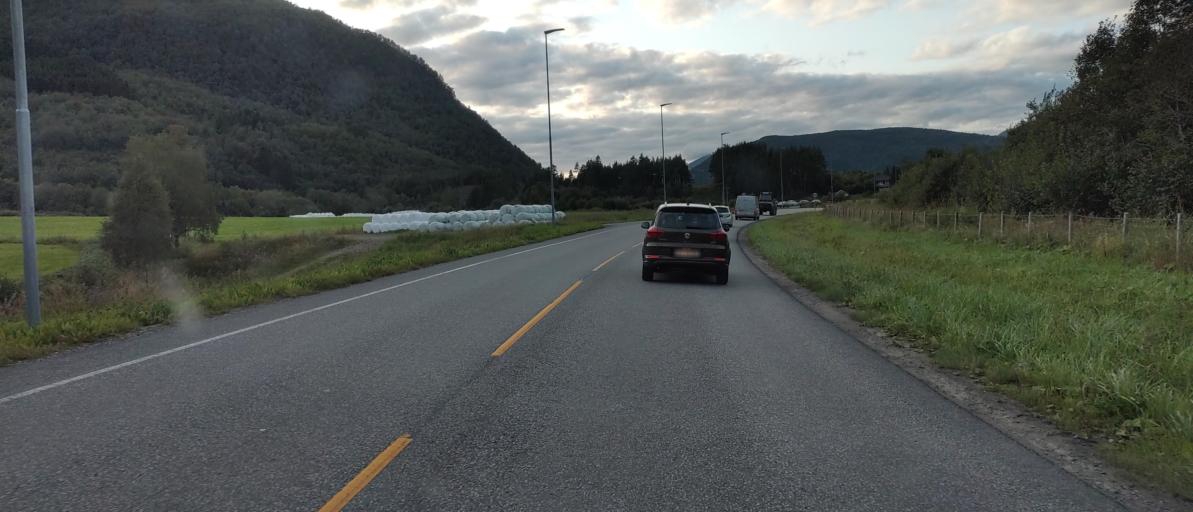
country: NO
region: More og Romsdal
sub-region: Molde
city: Molde
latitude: 62.7899
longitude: 7.2340
